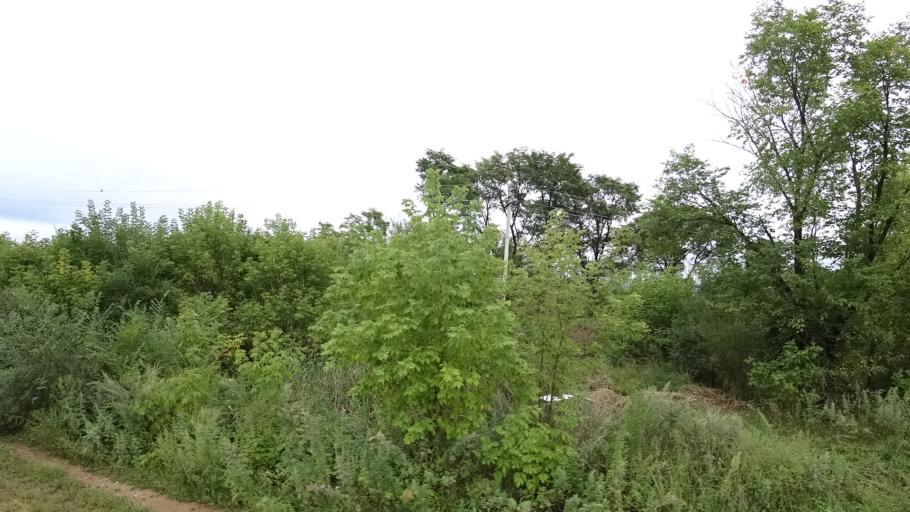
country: RU
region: Primorskiy
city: Rettikhovka
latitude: 44.1345
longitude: 132.6334
